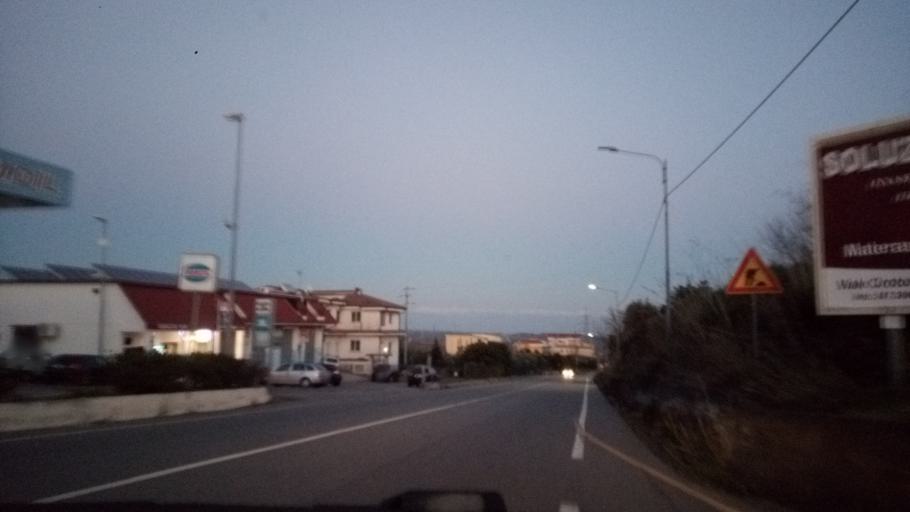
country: IT
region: Calabria
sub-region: Provincia di Catanzaro
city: Cava-Cuculera Nobile
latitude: 38.9050
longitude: 16.6130
